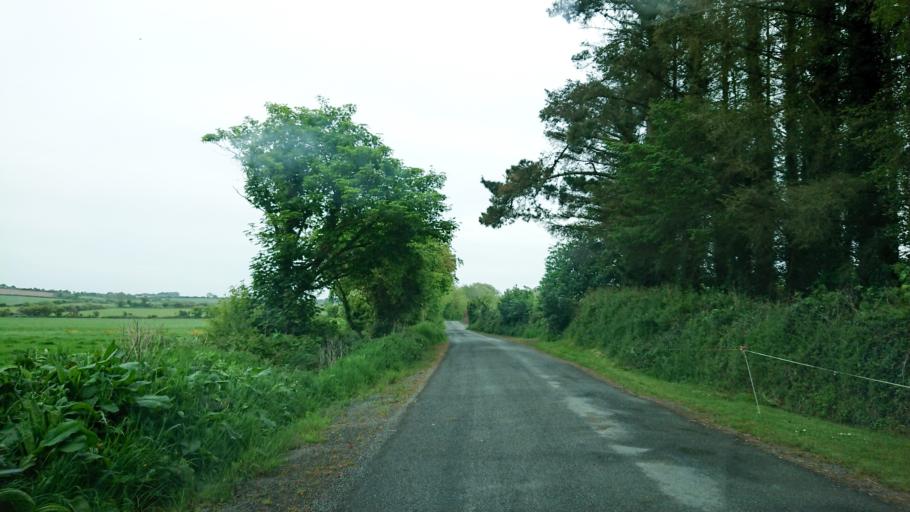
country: IE
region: Munster
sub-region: Waterford
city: Dunmore East
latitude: 52.2214
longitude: -7.0123
